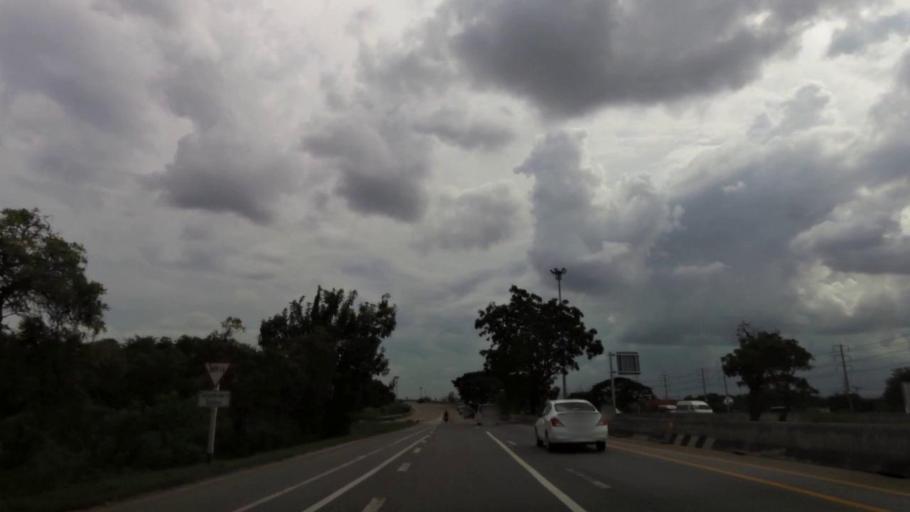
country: TH
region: Phra Nakhon Si Ayutthaya
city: Bang Pa-in
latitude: 14.1759
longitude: 100.6162
